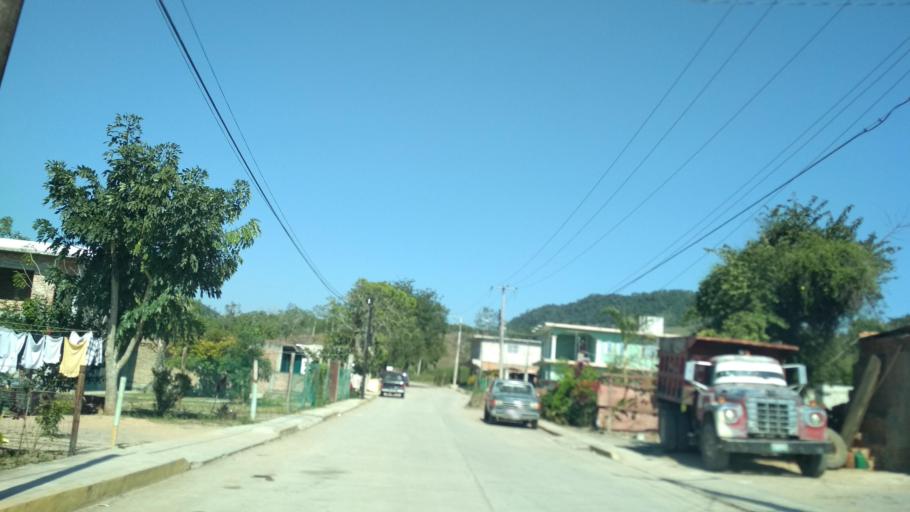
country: MX
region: Veracruz
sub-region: Papantla
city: El Chote
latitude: 20.3993
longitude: -97.3337
